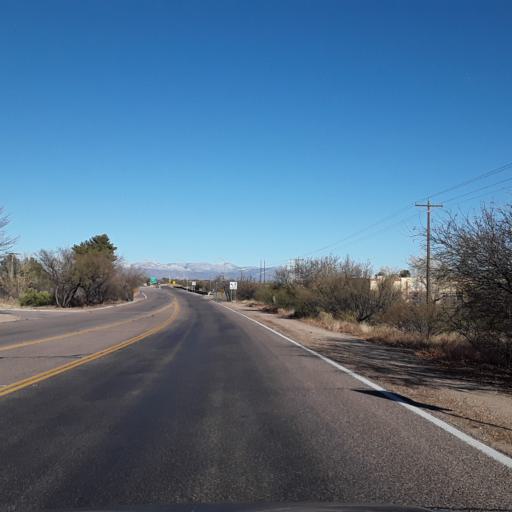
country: US
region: Arizona
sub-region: Cochise County
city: Sierra Vista
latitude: 31.5580
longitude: -110.3068
